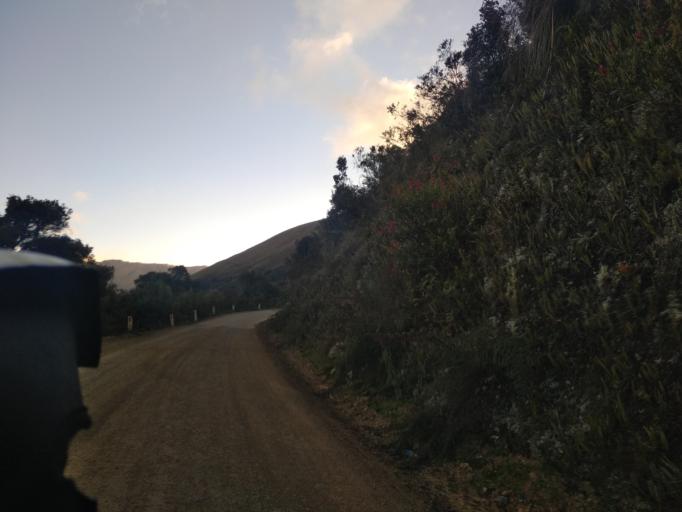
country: PE
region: Amazonas
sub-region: Provincia de Chachapoyas
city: Montevideo
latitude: -6.7203
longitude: -77.8758
